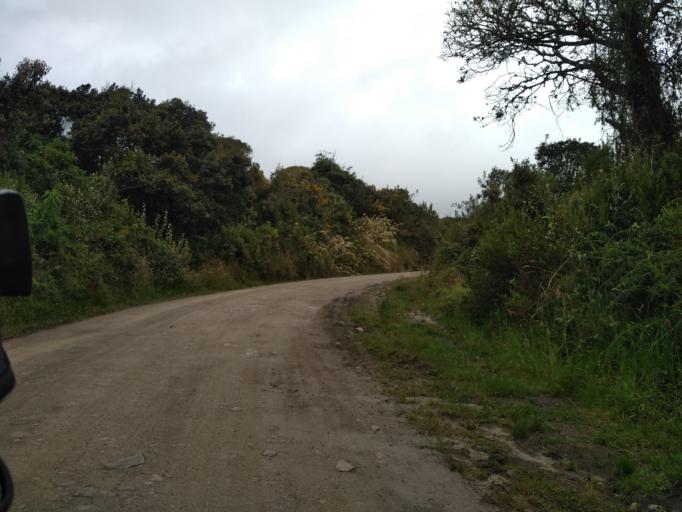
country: EC
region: Carchi
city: Tulcan
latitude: 0.7438
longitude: -77.7820
